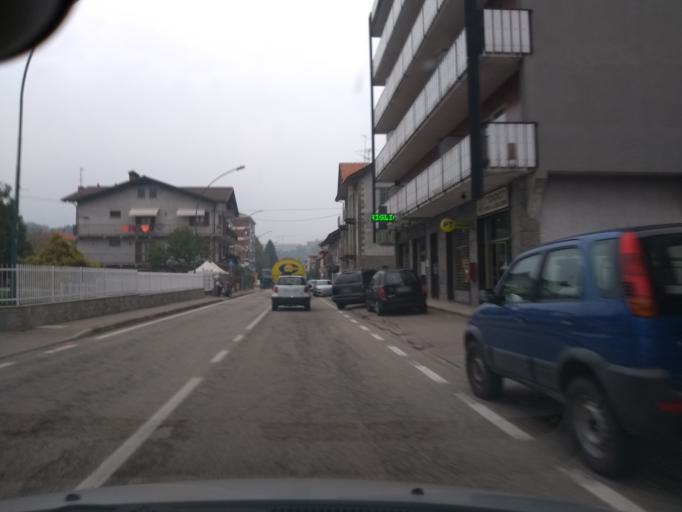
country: IT
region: Piedmont
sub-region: Provincia di Torino
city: Germagnano
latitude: 45.2634
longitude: 7.4702
